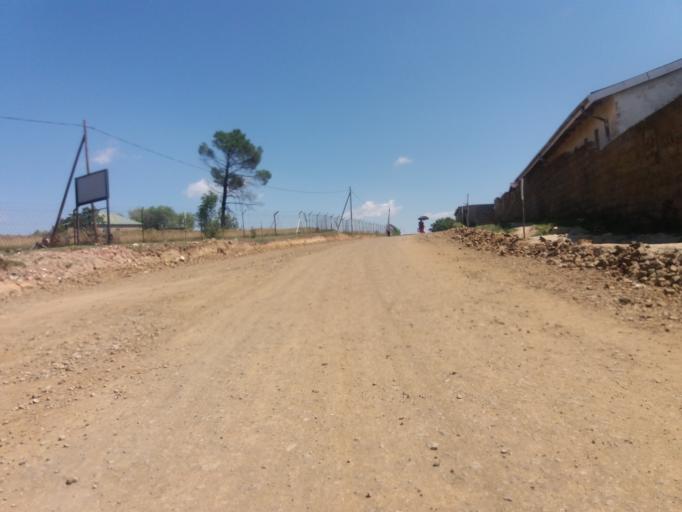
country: LS
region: Maseru
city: Maseru
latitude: -29.3173
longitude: 27.5040
